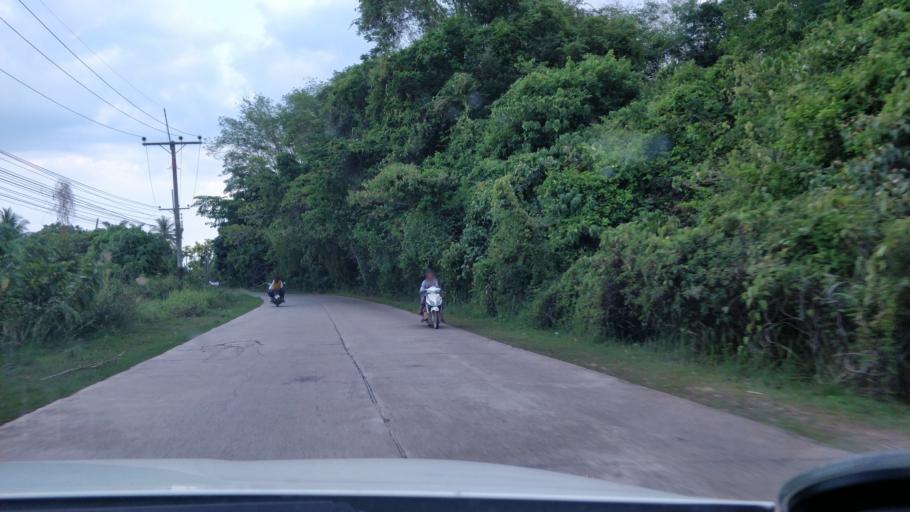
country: TH
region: Krabi
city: Saladan
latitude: 7.5791
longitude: 99.0678
